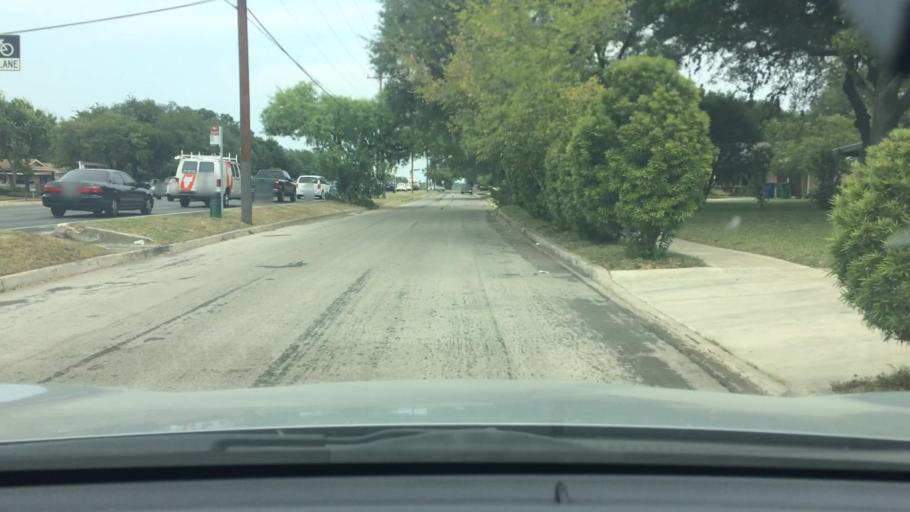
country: US
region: Texas
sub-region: Bexar County
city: Leon Valley
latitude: 29.4662
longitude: -98.6122
